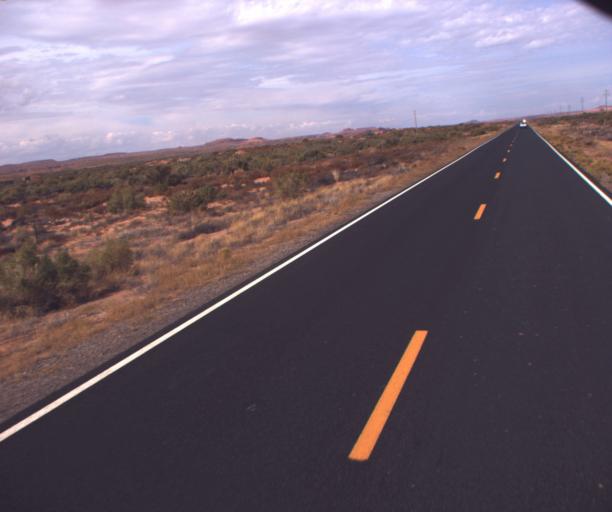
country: US
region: Arizona
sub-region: Apache County
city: Many Farms
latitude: 36.6425
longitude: -109.5892
